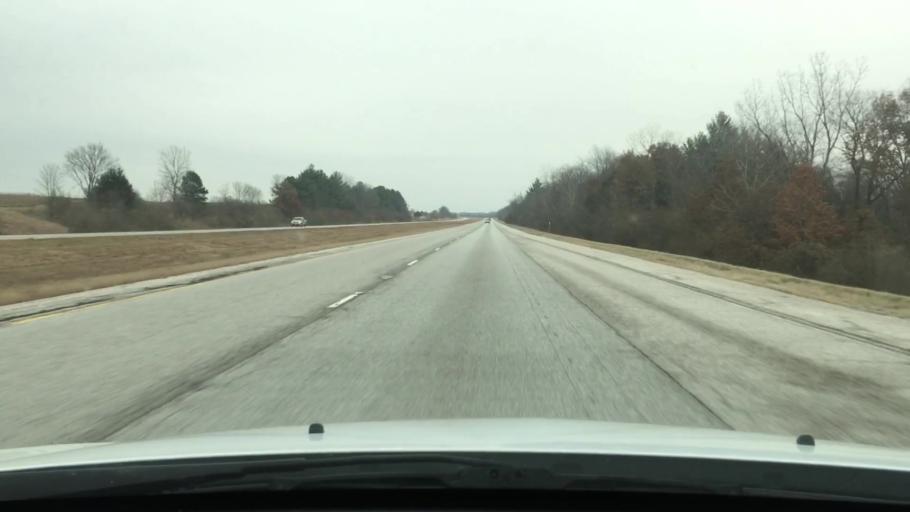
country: US
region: Illinois
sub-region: Morgan County
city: South Jacksonville
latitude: 39.6802
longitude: -90.2862
